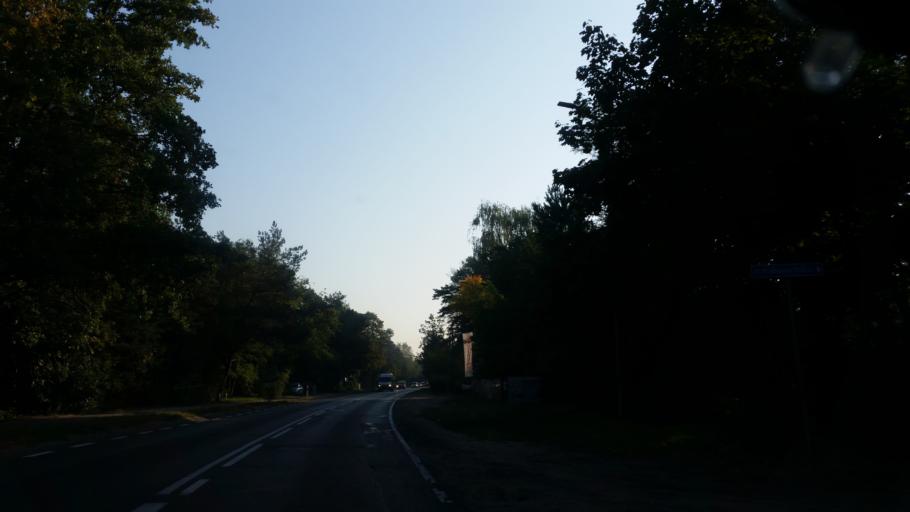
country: PL
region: Masovian Voivodeship
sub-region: Powiat otwocki
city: Jozefow
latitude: 52.1423
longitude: 21.2618
